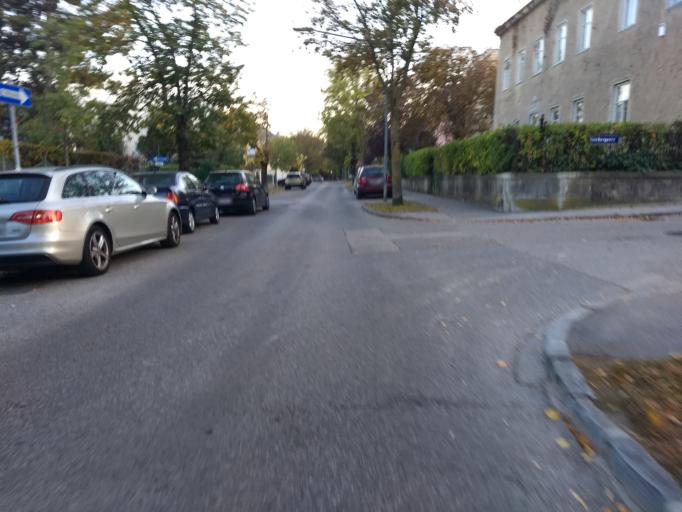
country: AT
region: Lower Austria
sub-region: Politischer Bezirk Modling
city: Perchtoldsdorf
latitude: 48.1254
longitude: 16.2579
